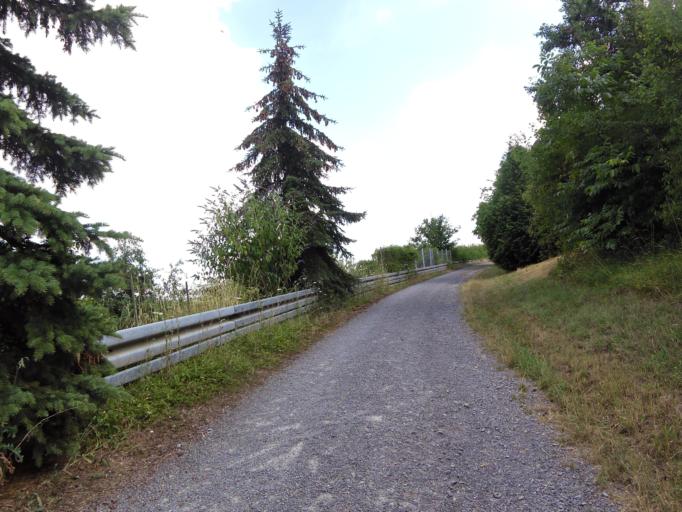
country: DE
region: Bavaria
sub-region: Regierungsbezirk Unterfranken
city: Randersacker
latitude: 49.7563
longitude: 9.9654
